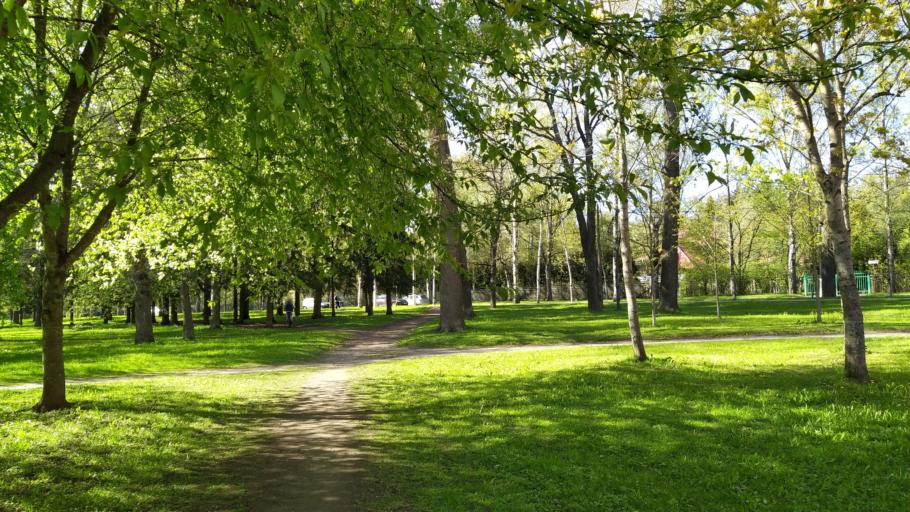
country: RU
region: St.-Petersburg
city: Pavlovsk
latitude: 59.6879
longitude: 30.4395
